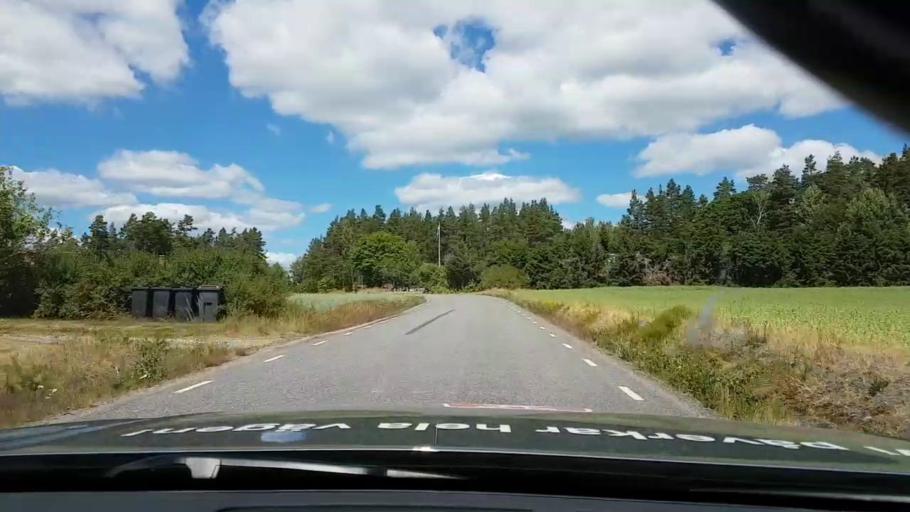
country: SE
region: Kalmar
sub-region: Vasterviks Kommun
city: Forserum
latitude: 58.0176
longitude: 16.5763
